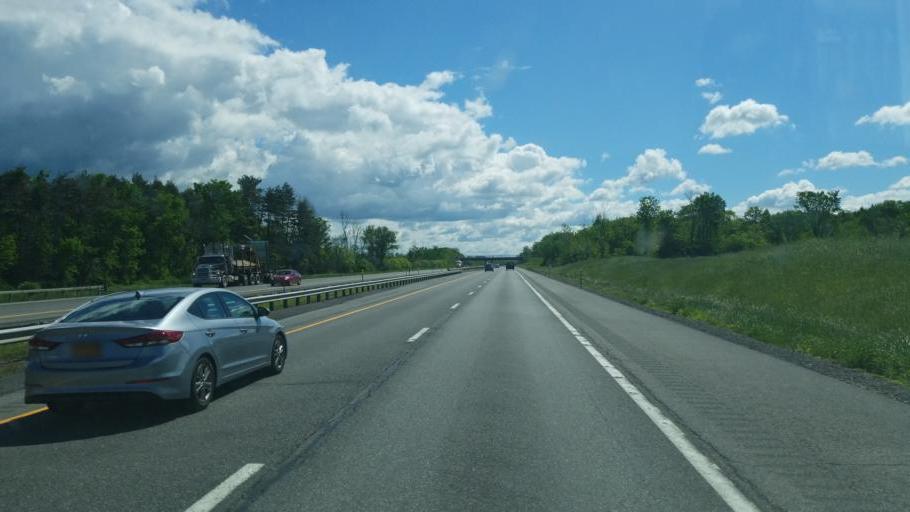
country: US
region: New York
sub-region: Oneida County
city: Vernon
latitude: 43.1332
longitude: -75.5070
